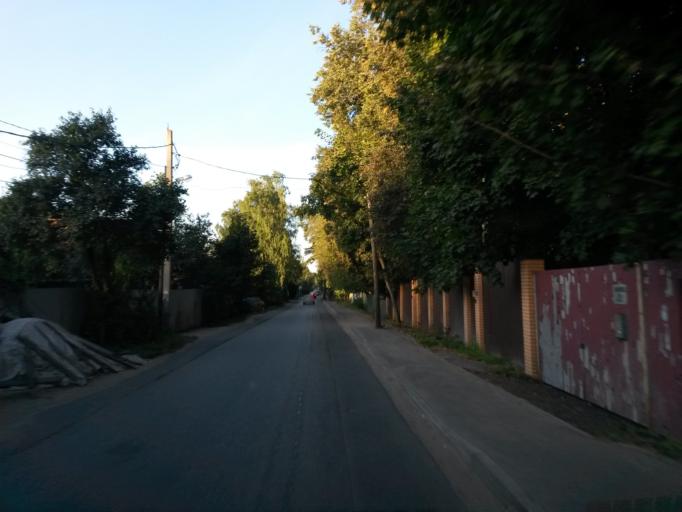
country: RU
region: Moskovskaya
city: Mamontovka
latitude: 55.9858
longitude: 37.8461
